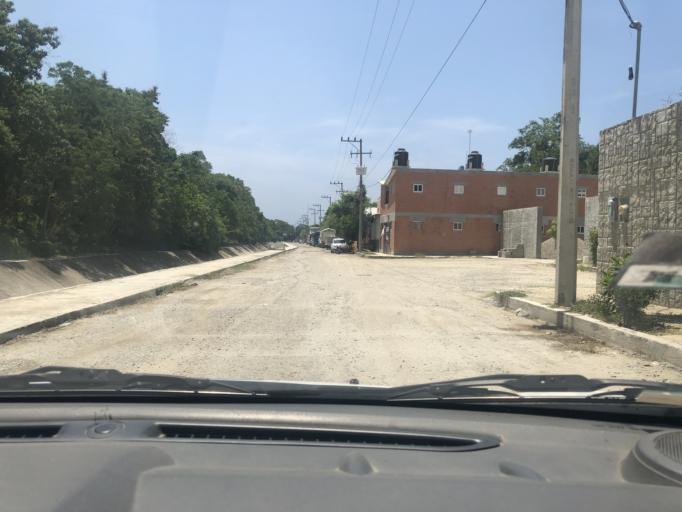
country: MX
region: Oaxaca
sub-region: Santa Maria Huatulco
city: Sector H Tres
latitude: 15.7797
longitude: -96.1523
